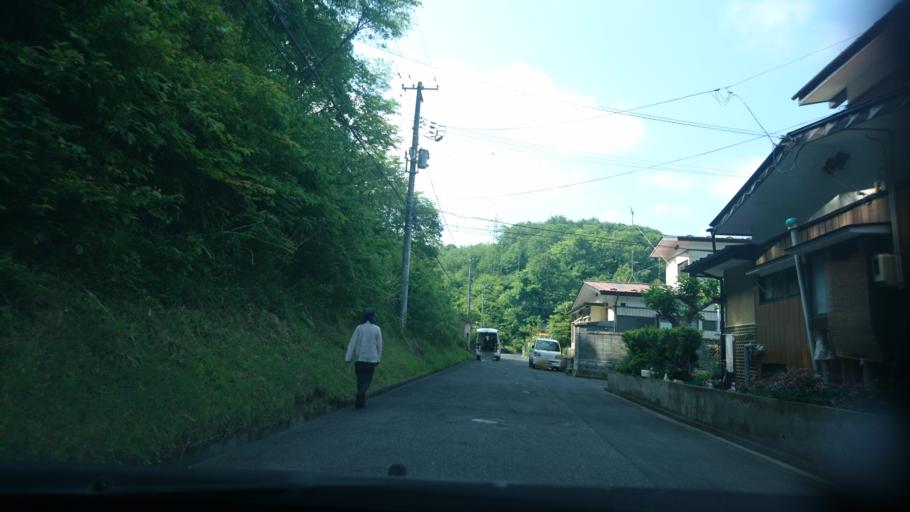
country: JP
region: Iwate
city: Ichinoseki
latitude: 38.9065
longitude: 141.1483
